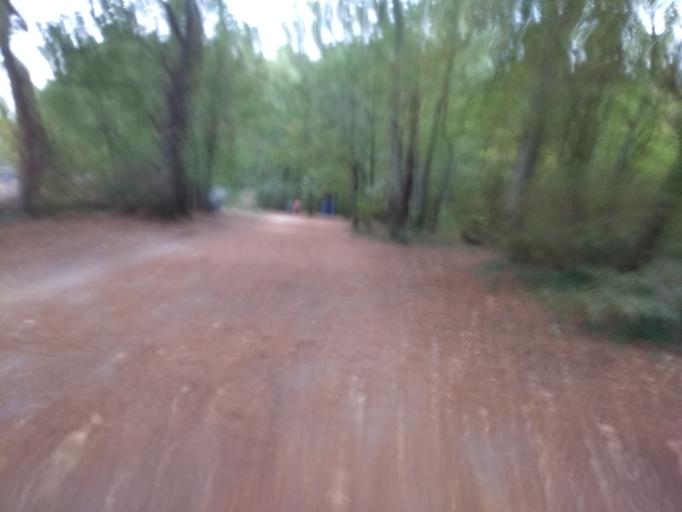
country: FR
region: Aquitaine
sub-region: Departement de la Gironde
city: Pessac
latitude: 44.8187
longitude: -0.6469
